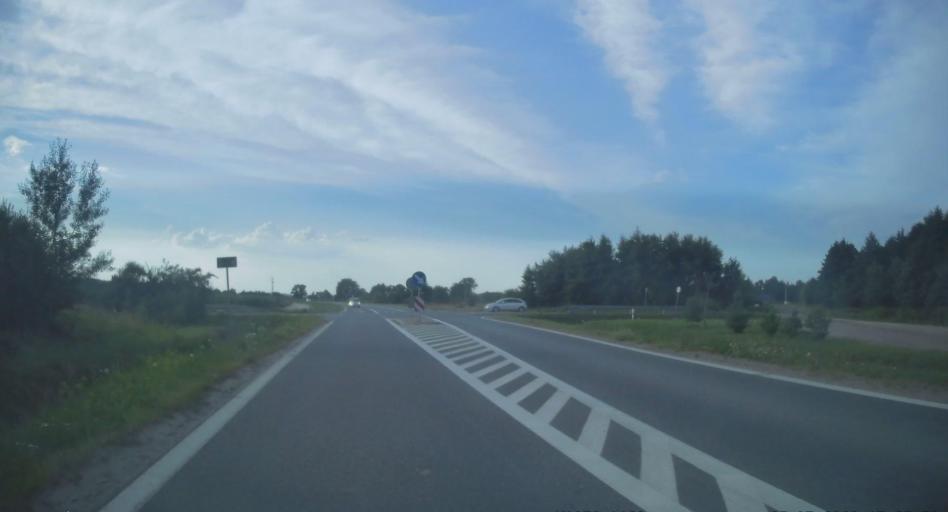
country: PL
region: Lesser Poland Voivodeship
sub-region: Powiat brzeski
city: Szczurowa
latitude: 50.0836
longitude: 20.6320
